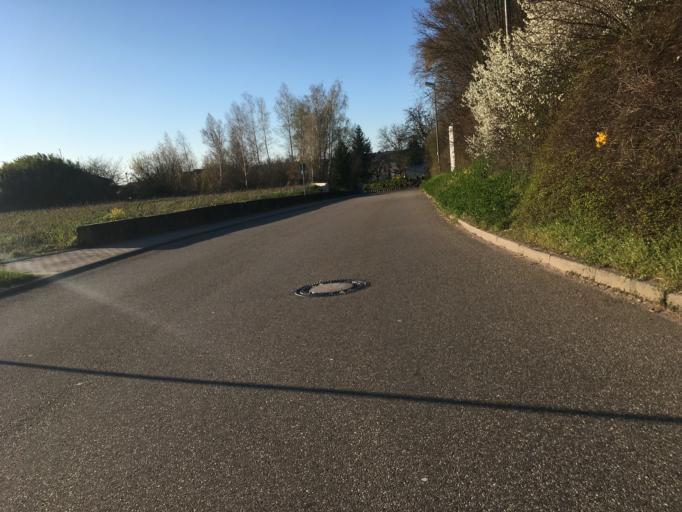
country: DE
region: Baden-Wuerttemberg
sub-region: Regierungsbezirk Stuttgart
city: Schwaigern
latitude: 49.1379
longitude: 9.0668
